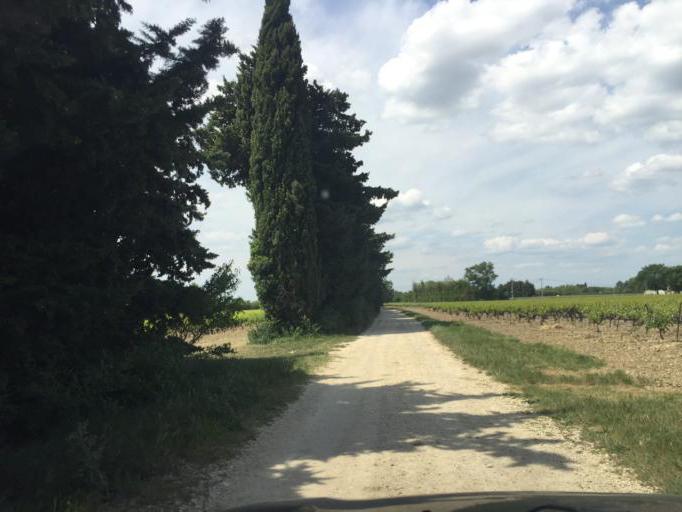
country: FR
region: Provence-Alpes-Cote d'Azur
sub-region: Departement du Vaucluse
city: Jonquieres
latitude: 44.1336
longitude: 4.9052
